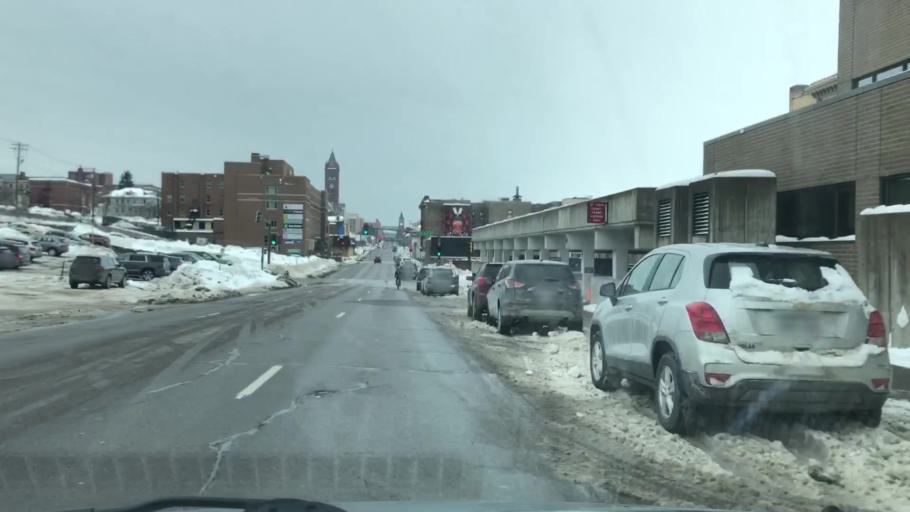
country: US
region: Minnesota
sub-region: Saint Louis County
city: Duluth
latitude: 46.7848
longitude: -92.1049
